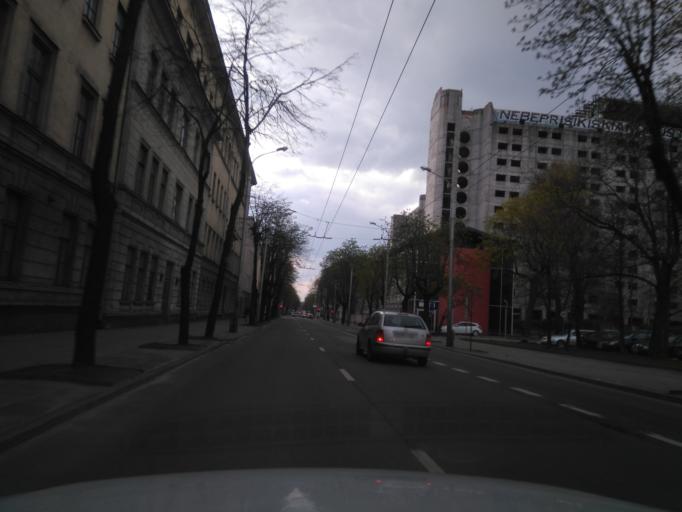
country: LT
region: Kauno apskritis
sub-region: Kaunas
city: Kaunas
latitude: 54.8955
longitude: 23.9203
